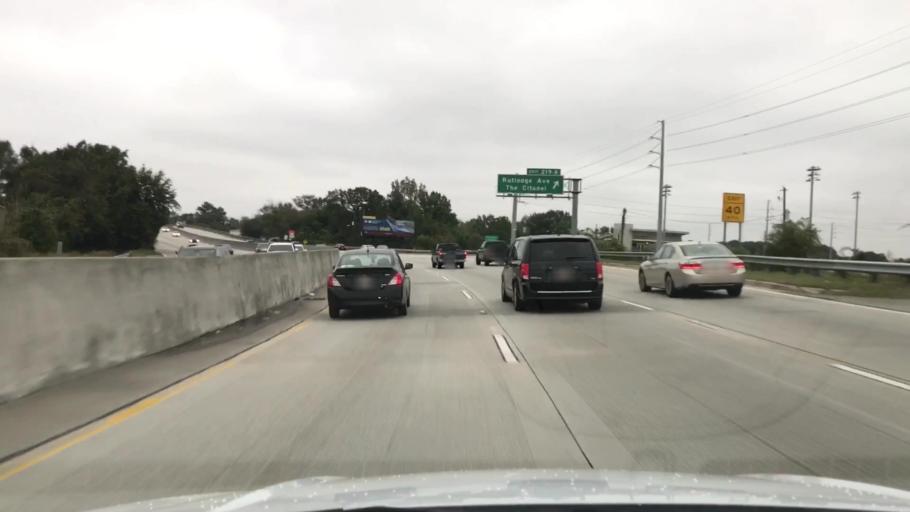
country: US
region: South Carolina
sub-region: Charleston County
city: North Charleston
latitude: 32.8193
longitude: -79.9551
